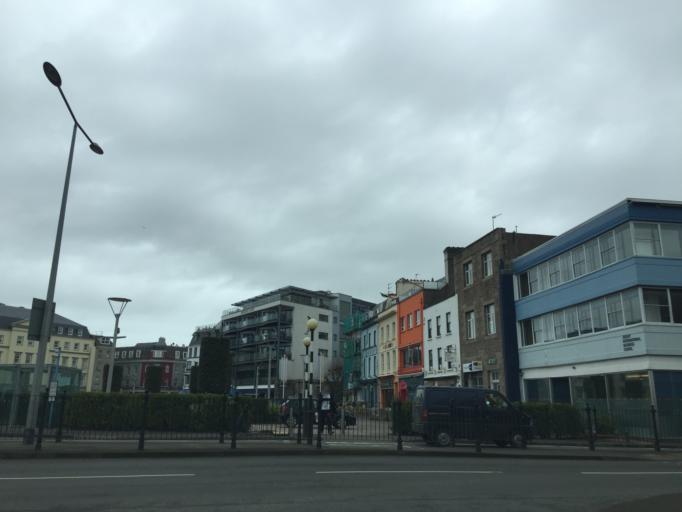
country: JE
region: St Helier
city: Saint Helier
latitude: 49.1817
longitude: -2.1082
